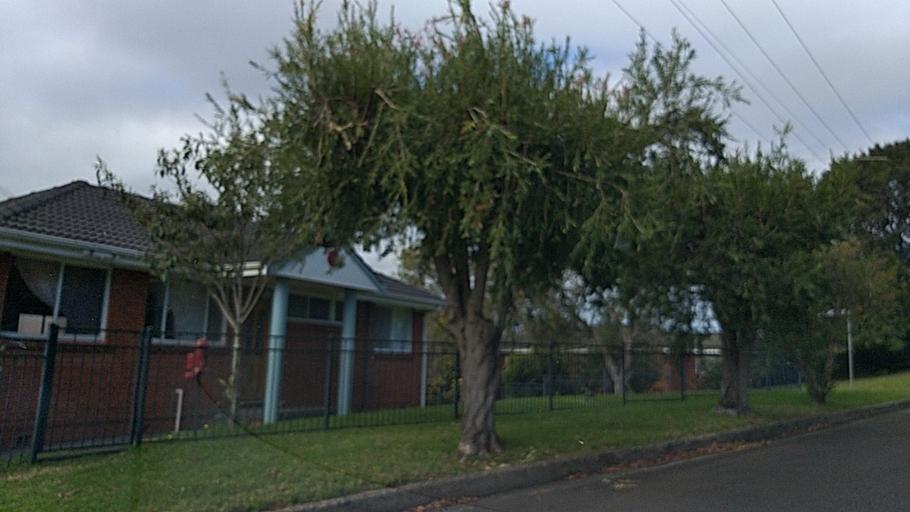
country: AU
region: New South Wales
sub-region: Wollongong
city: Mount Ousley
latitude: -34.3963
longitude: 150.8785
